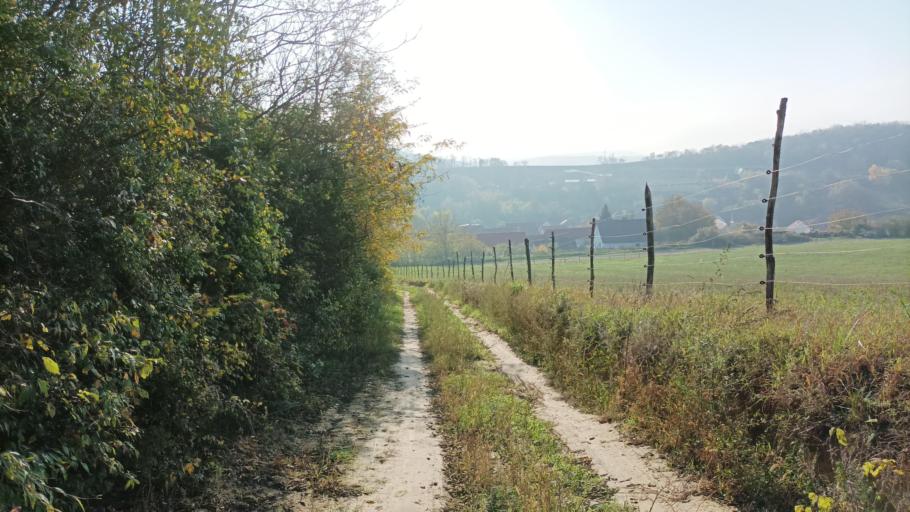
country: HU
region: Tolna
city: Szentgalpuszta
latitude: 46.3427
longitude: 18.6017
